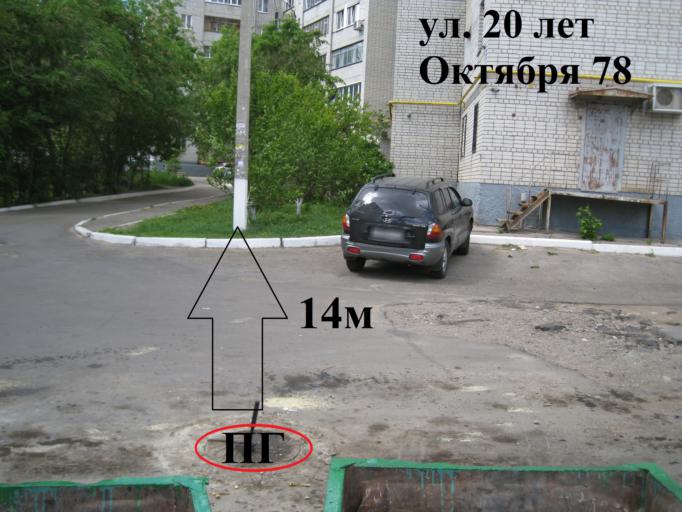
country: RU
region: Voronezj
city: Voronezh
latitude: 51.6501
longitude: 39.1956
